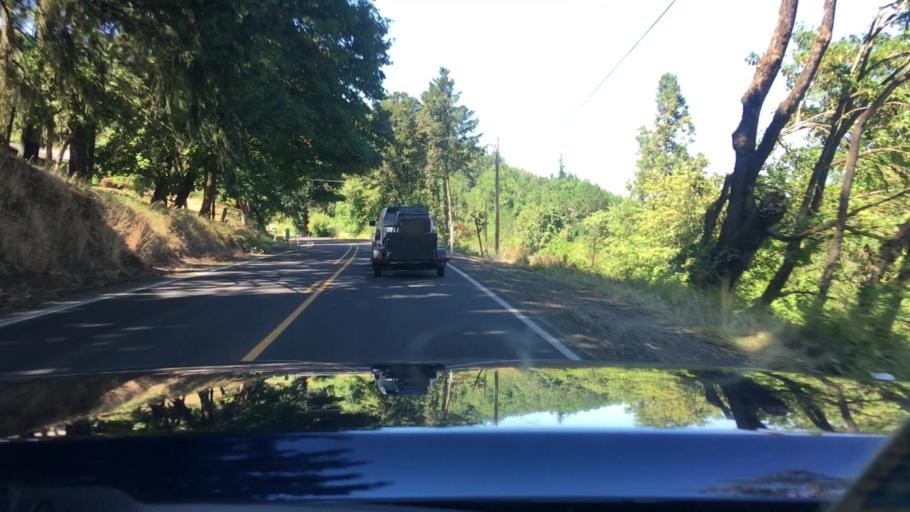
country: US
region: Oregon
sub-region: Lane County
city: Cottage Grove
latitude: 43.8186
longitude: -123.0461
